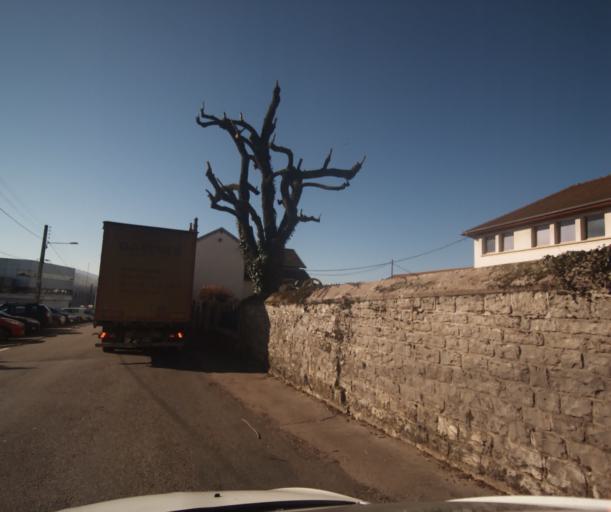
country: FR
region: Franche-Comte
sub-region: Departement du Doubs
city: Besancon
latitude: 47.2418
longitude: 5.9997
